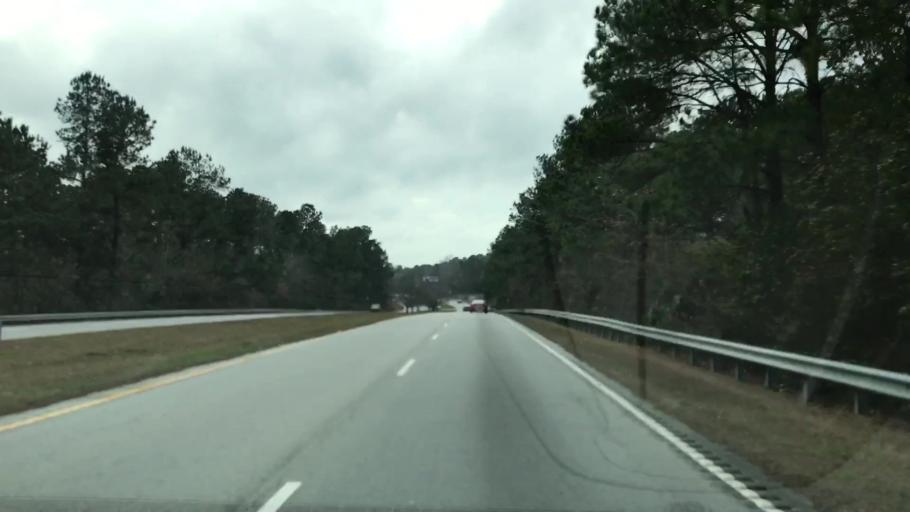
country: US
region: South Carolina
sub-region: Berkeley County
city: Moncks Corner
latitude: 33.1855
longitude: -80.0090
